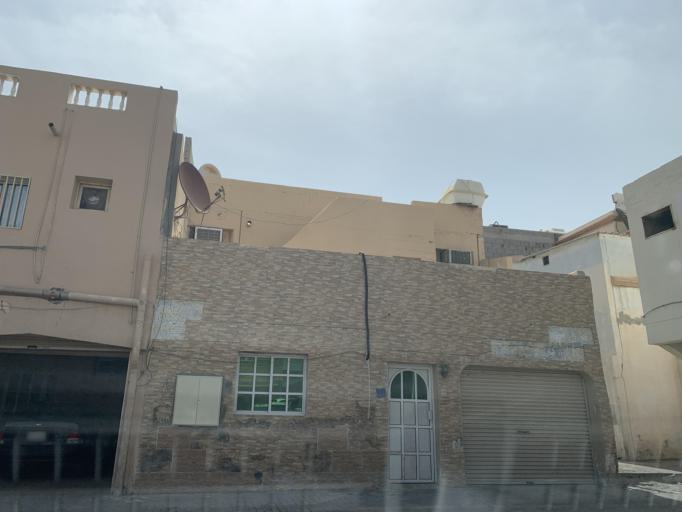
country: BH
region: Northern
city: Madinat `Isa
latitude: 26.1682
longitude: 50.5613
